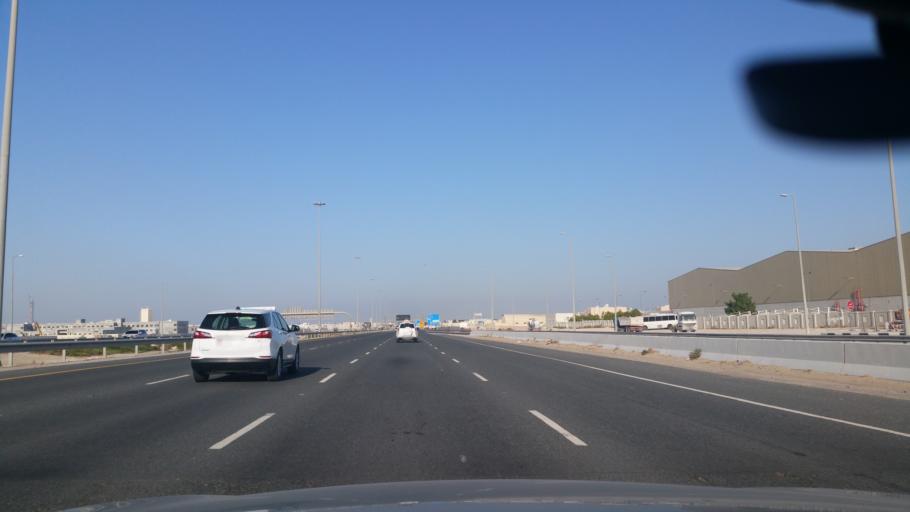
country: QA
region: Baladiyat ar Rayyan
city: Ar Rayyan
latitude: 25.2133
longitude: 51.4113
